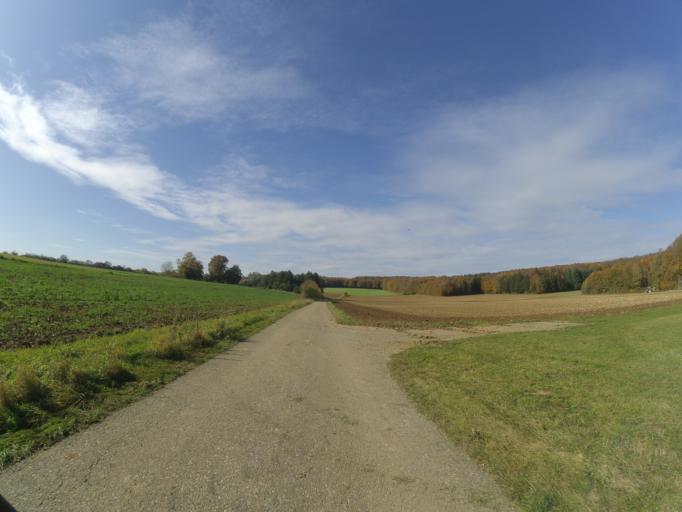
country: DE
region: Baden-Wuerttemberg
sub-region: Tuebingen Region
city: Westerstetten
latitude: 48.5418
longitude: 9.9673
